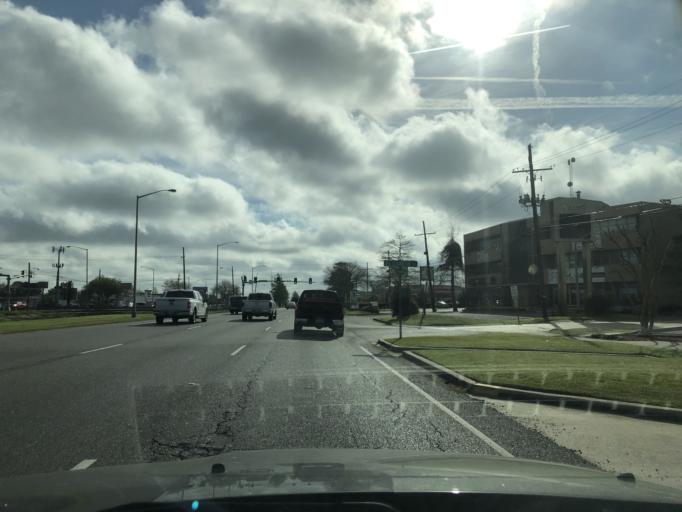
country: US
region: Louisiana
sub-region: Jefferson Parish
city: Kenner
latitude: 30.0060
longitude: -90.2023
